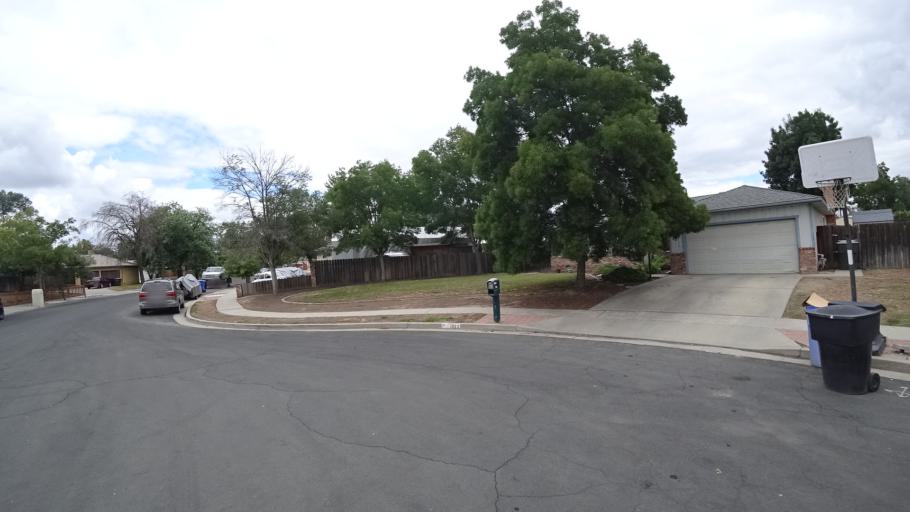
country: US
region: California
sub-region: Kings County
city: Hanford
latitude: 36.3369
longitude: -119.6593
